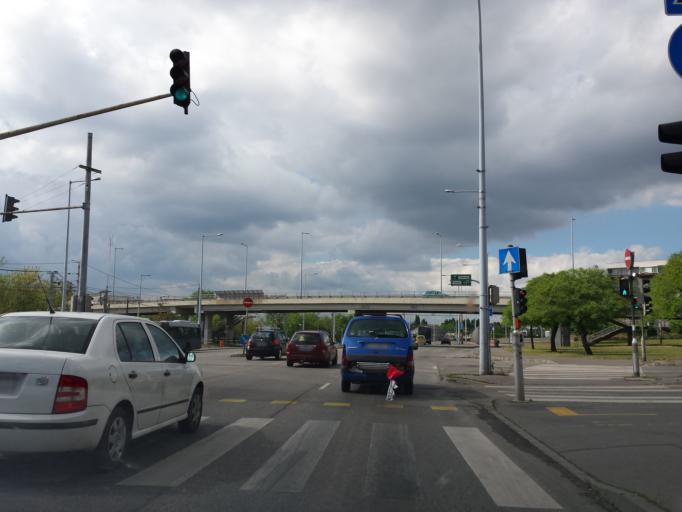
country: HU
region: Budapest
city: Budapest XX. keruelet
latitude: 47.4359
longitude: 19.0957
